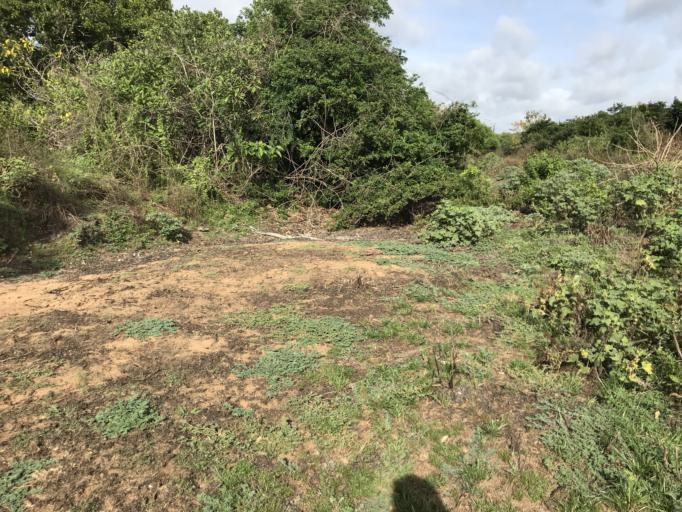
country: LK
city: Padaviya Divisional Secretariat
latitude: 9.0878
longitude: 80.8074
